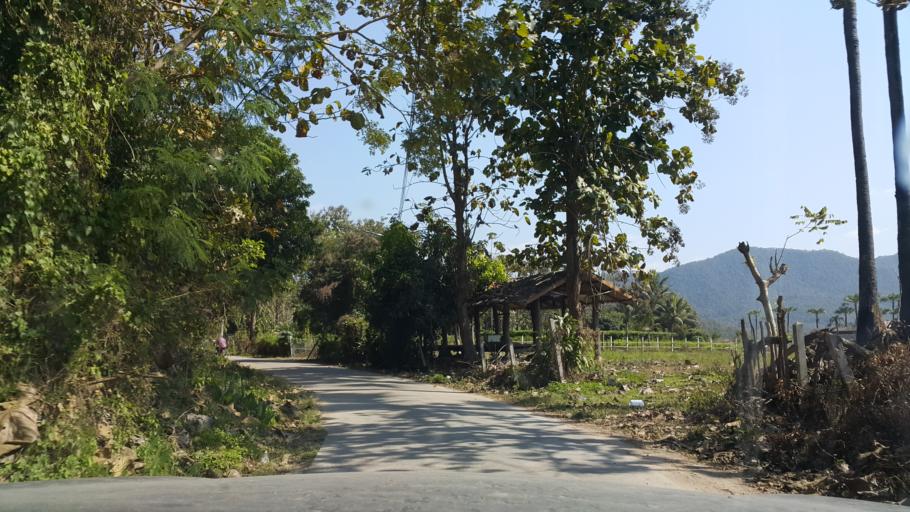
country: TH
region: Chiang Mai
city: Mae On
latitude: 18.7283
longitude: 99.2123
